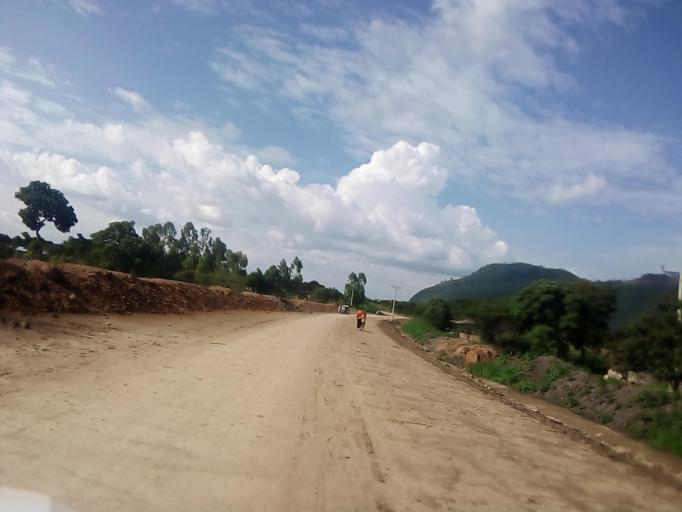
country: ET
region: Southern Nations, Nationalities, and People's Region
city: K'olito
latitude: 7.6202
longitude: 38.0638
